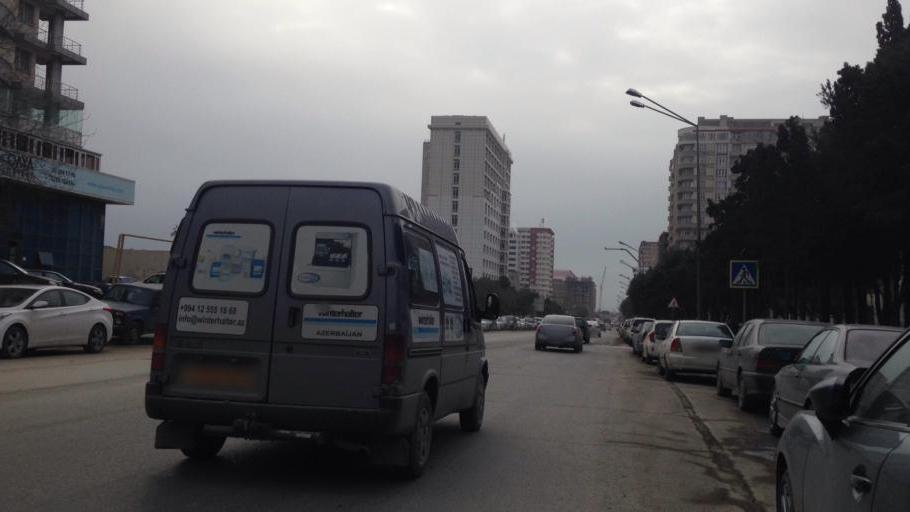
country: AZ
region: Baki
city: Baku
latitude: 40.3879
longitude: 49.8758
